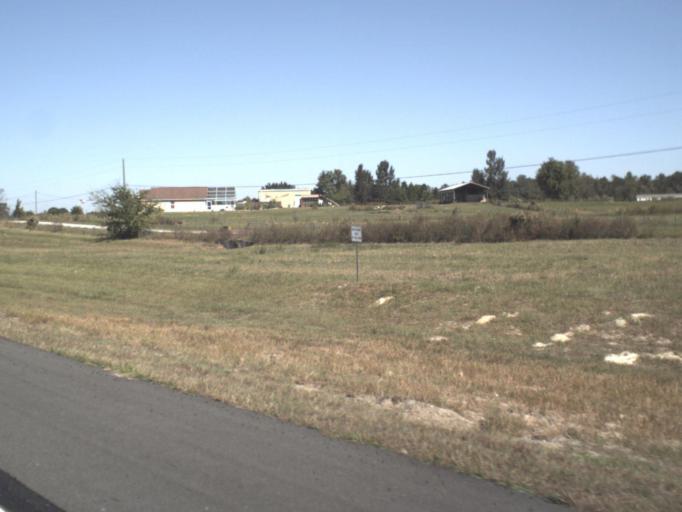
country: US
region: Florida
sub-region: Hernando County
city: Brookridge
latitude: 28.5881
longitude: -82.4819
